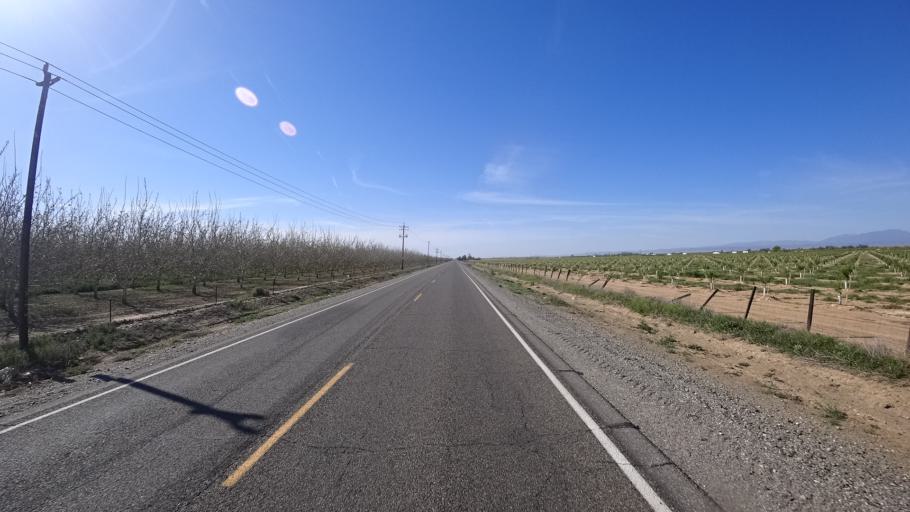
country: US
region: California
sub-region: Glenn County
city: Orland
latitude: 39.6657
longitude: -122.1970
